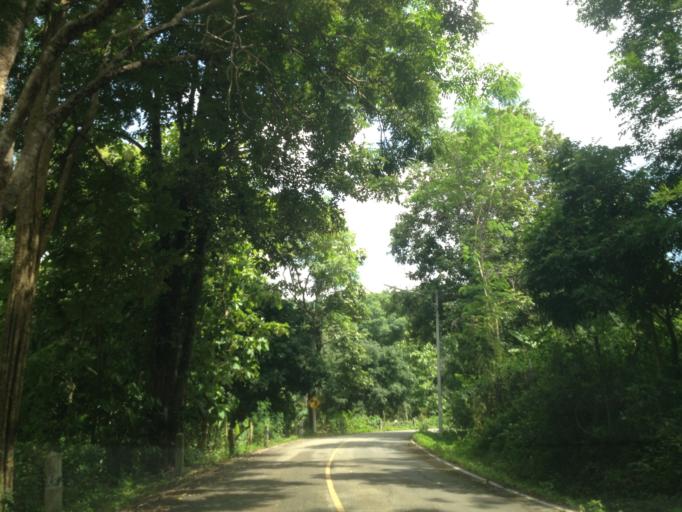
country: TH
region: Chiang Mai
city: Hang Dong
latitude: 18.7594
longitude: 98.9049
